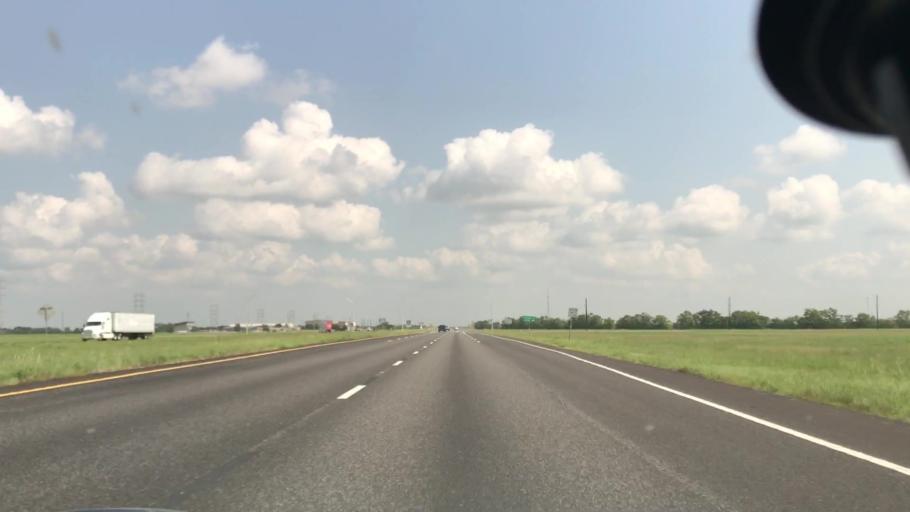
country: US
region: Texas
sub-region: Brazoria County
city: Rosharon
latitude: 29.4094
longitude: -95.4269
